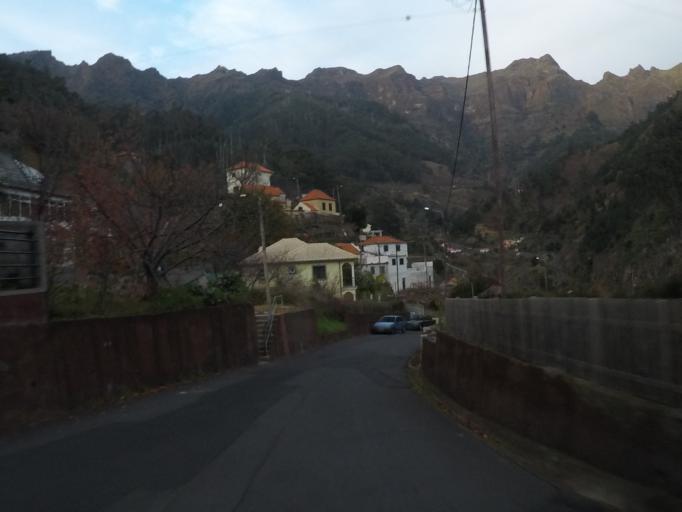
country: PT
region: Madeira
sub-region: Camara de Lobos
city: Curral das Freiras
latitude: 32.7327
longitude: -16.9709
